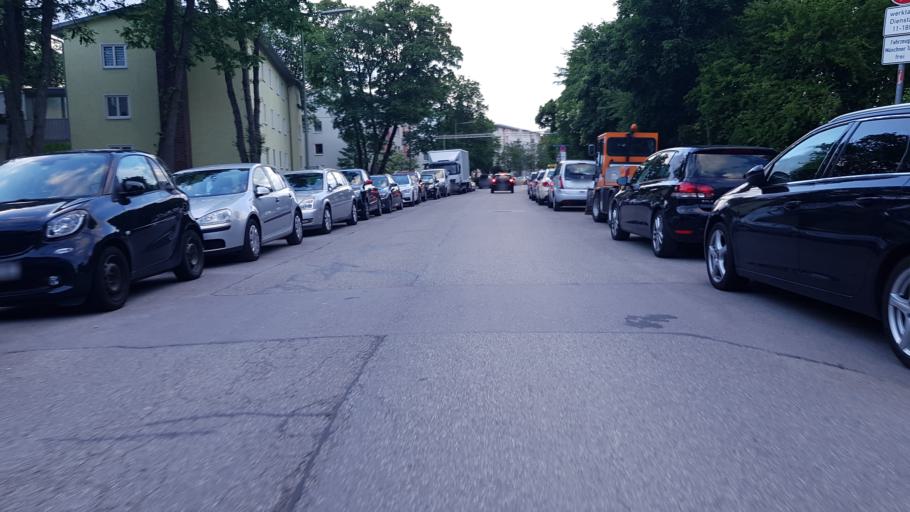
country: DE
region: Bavaria
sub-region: Upper Bavaria
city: Pasing
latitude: 48.1260
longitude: 11.4932
